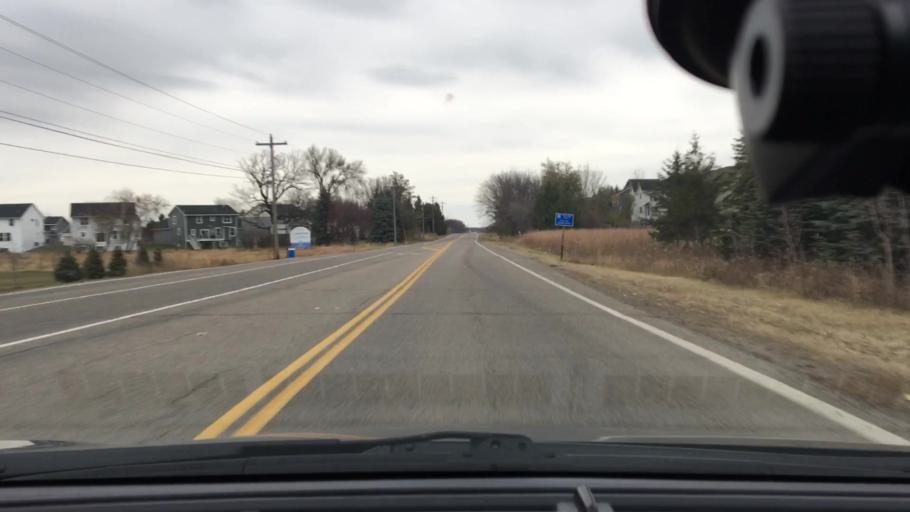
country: US
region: Minnesota
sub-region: Hennepin County
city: Corcoran
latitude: 45.0732
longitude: -93.5220
